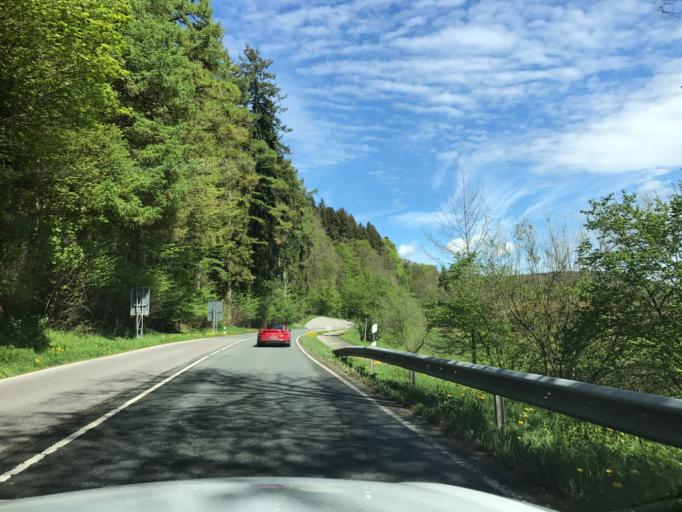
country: DE
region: Bavaria
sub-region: Upper Bavaria
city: Bad Wiessee
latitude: 47.7279
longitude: 11.7168
